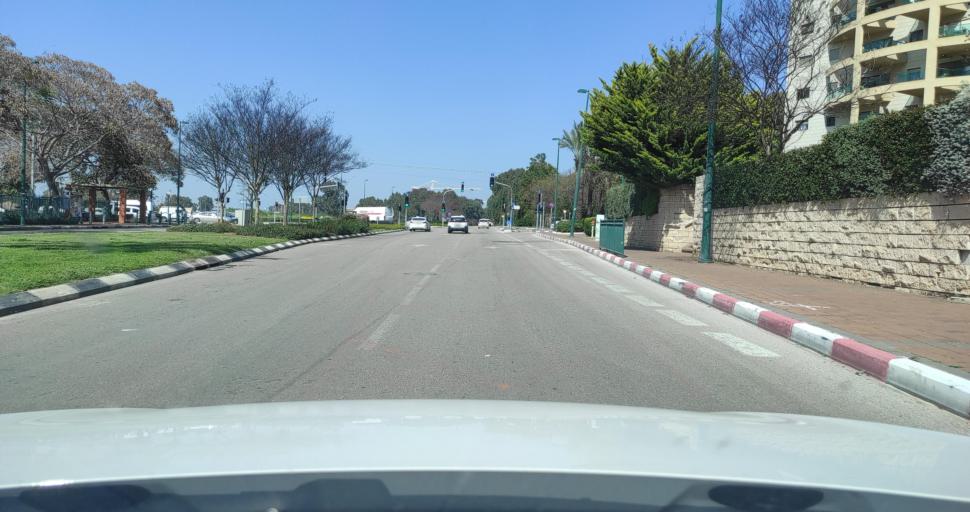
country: IL
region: Central District
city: Nordiyya
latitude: 32.3101
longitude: 34.8757
